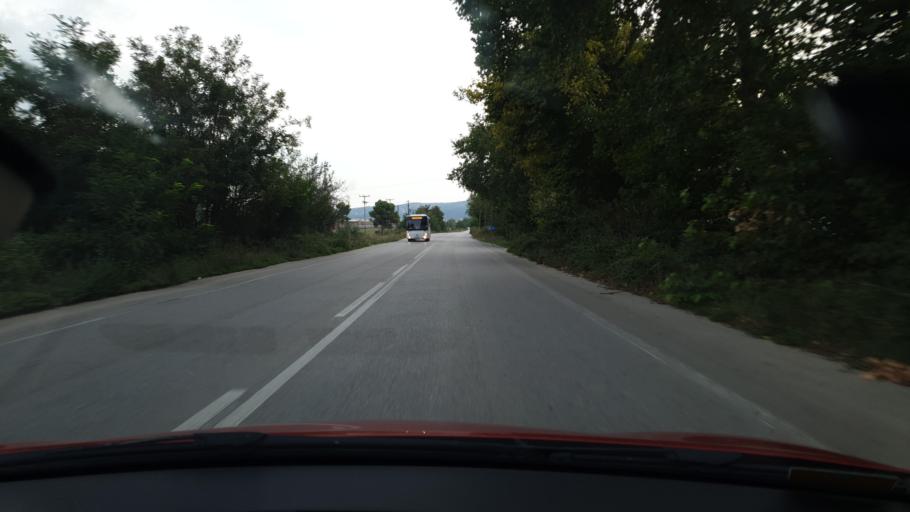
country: GR
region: Central Macedonia
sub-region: Nomos Thessalonikis
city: Liti
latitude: 40.7811
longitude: 23.0005
